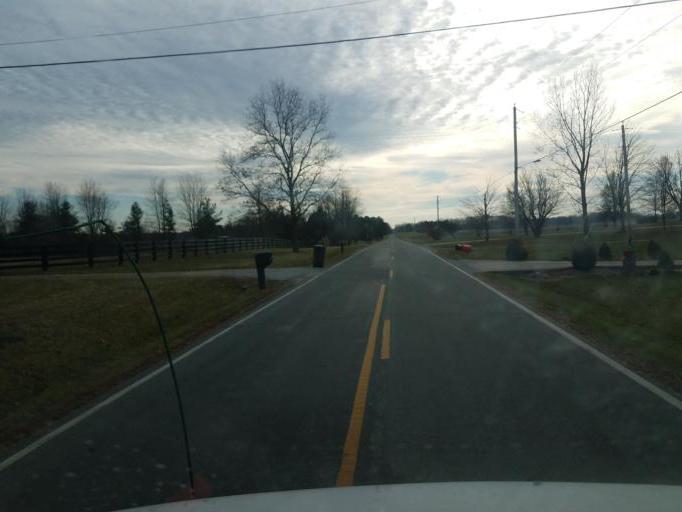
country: US
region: Ohio
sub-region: Delaware County
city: Ashley
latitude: 40.3211
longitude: -82.9588
